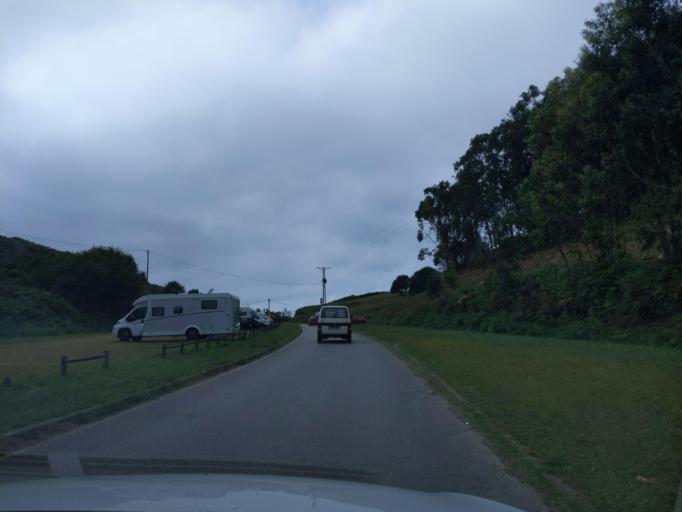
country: ES
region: Asturias
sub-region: Province of Asturias
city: Aviles
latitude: 43.5998
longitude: -5.9150
